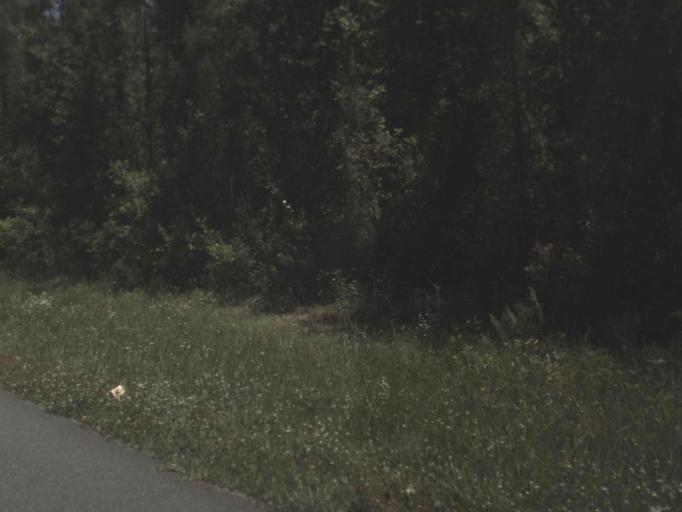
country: US
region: Florida
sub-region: Baker County
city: Macclenny
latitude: 30.2563
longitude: -82.2584
